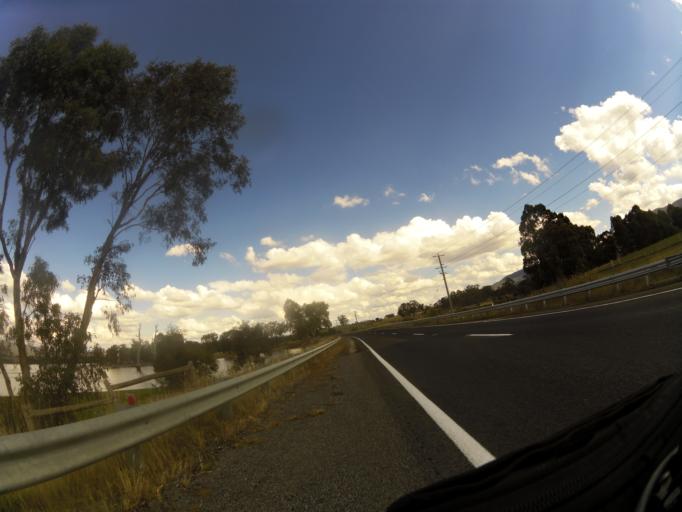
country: AU
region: Victoria
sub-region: Mansfield
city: Mansfield
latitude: -36.9035
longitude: 145.9969
